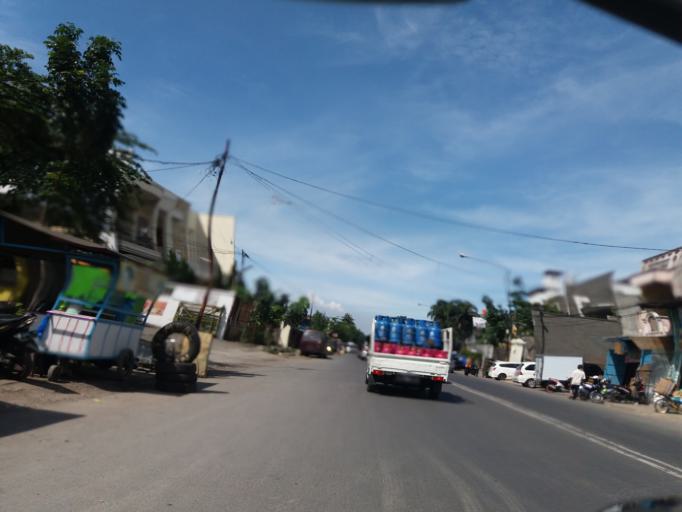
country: ID
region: West Java
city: Bandung
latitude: -6.9258
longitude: 107.5902
